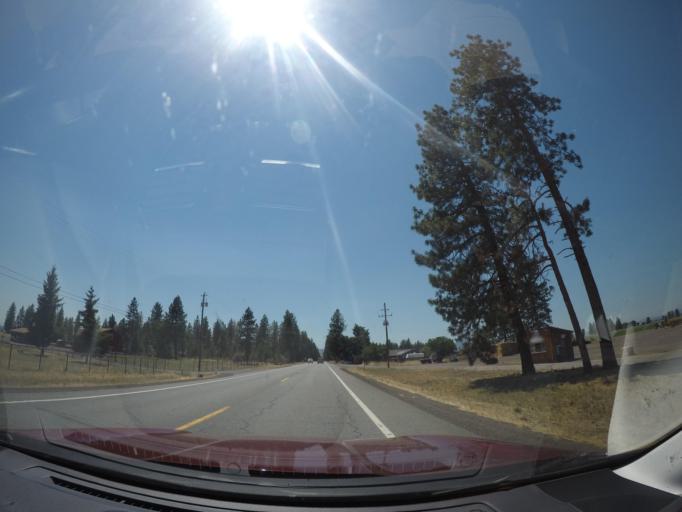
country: US
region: California
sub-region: Shasta County
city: Burney
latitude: 41.0657
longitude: -121.3545
